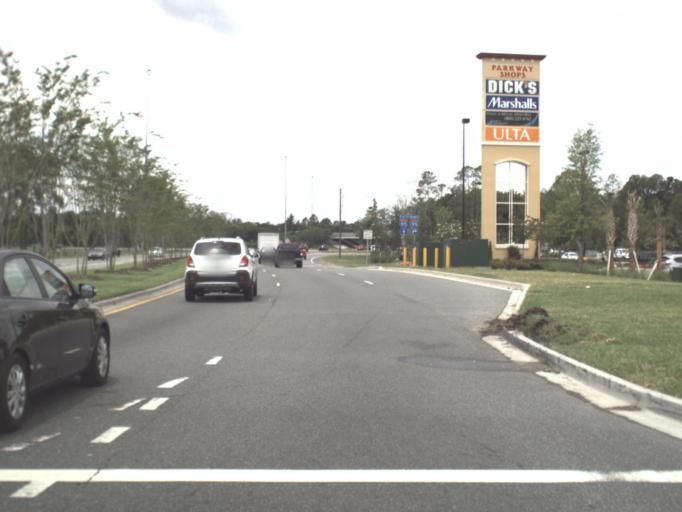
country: US
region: Florida
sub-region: Duval County
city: Jacksonville
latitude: 30.4814
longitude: -81.6392
